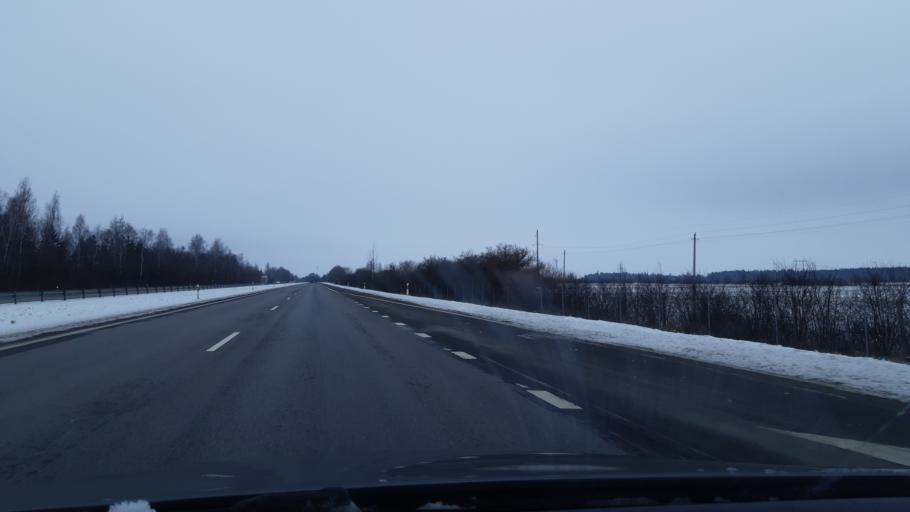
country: LT
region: Kauno apskritis
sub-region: Kaunas
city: Sargenai
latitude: 55.0746
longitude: 23.8143
